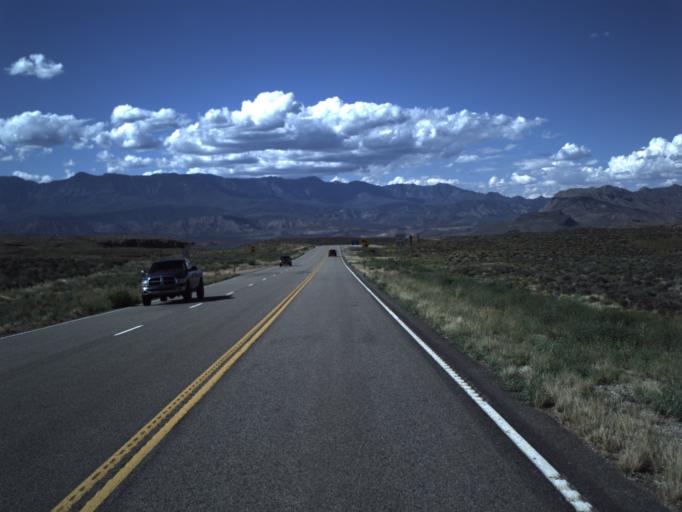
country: US
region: Utah
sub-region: Washington County
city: Hurricane
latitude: 37.1598
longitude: -113.2606
